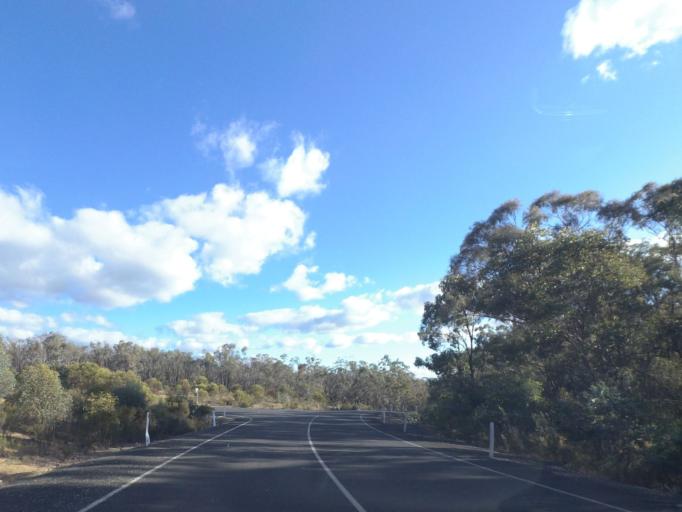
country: AU
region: Victoria
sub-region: Mount Alexander
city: Castlemaine
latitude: -37.1557
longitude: 144.2312
